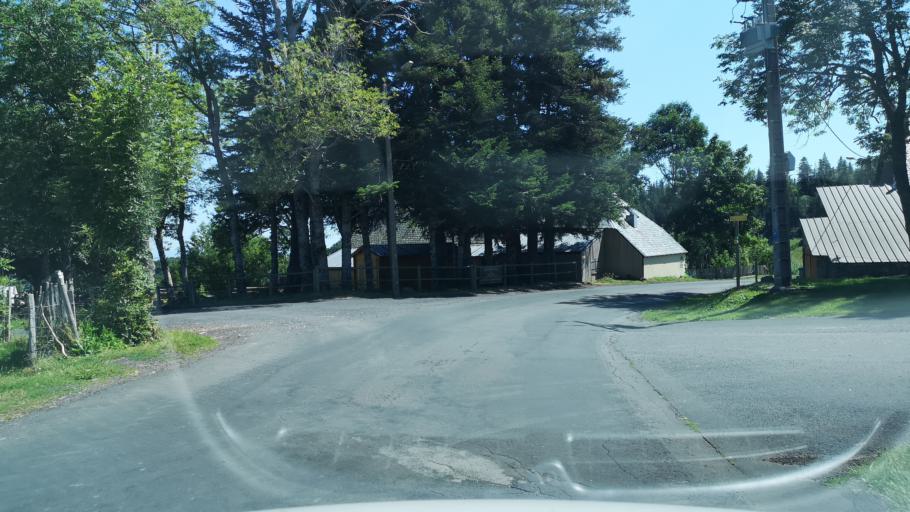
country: FR
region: Auvergne
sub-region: Departement du Puy-de-Dome
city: Mont-Dore
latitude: 45.5466
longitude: 2.9013
